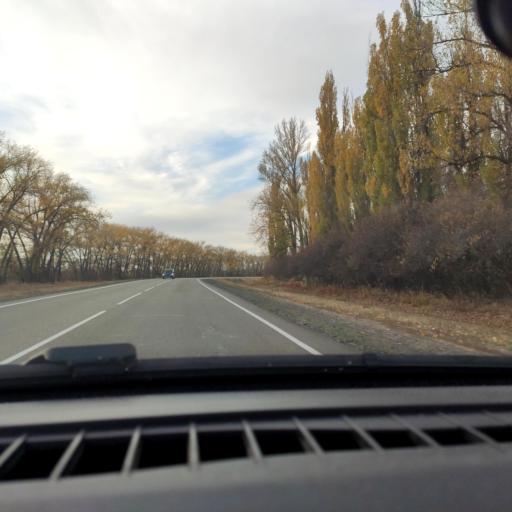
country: RU
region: Voronezj
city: Ostrogozhsk
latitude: 50.9723
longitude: 38.9983
